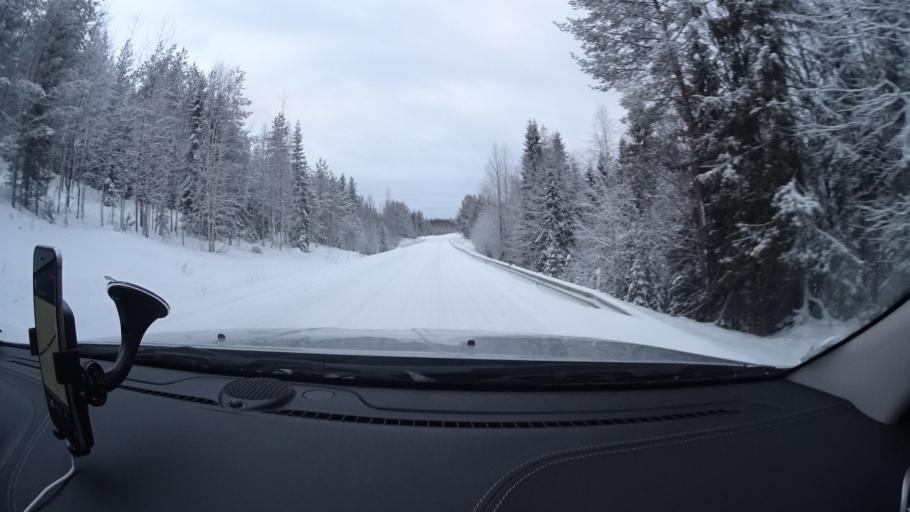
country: FI
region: Lapland
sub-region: Itae-Lappi
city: Kemijaervi
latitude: 66.3293
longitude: 27.0371
